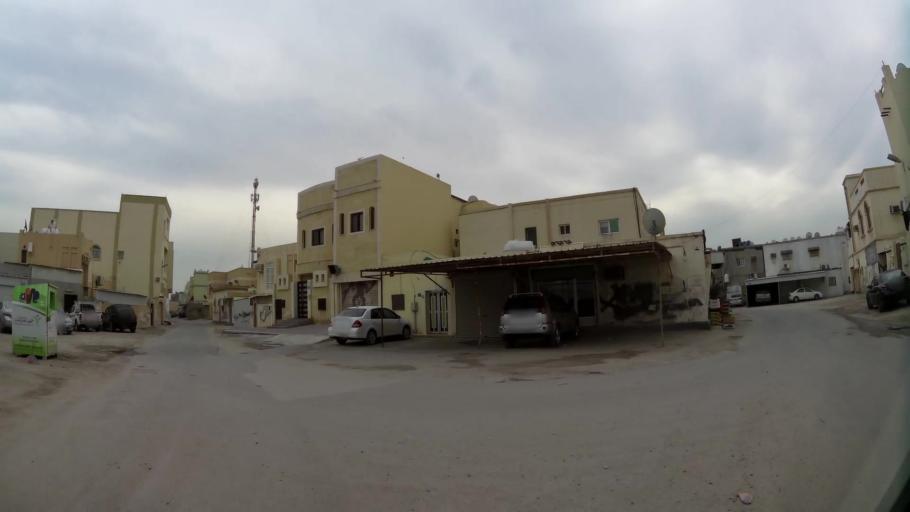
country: BH
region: Northern
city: Sitrah
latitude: 26.1447
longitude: 50.6106
